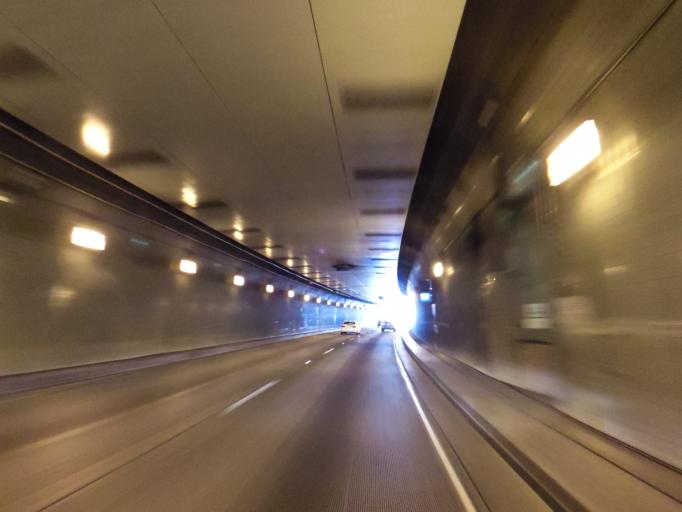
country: US
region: California
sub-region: Alameda County
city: Piedmont
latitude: 37.8555
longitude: -122.2165
